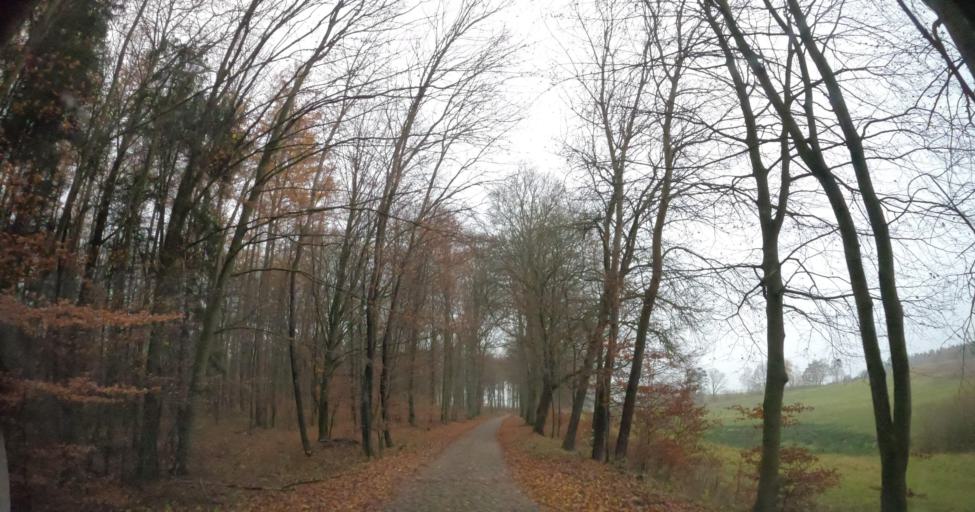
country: PL
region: West Pomeranian Voivodeship
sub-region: Powiat drawski
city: Drawsko Pomorskie
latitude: 53.5577
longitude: 15.7243
